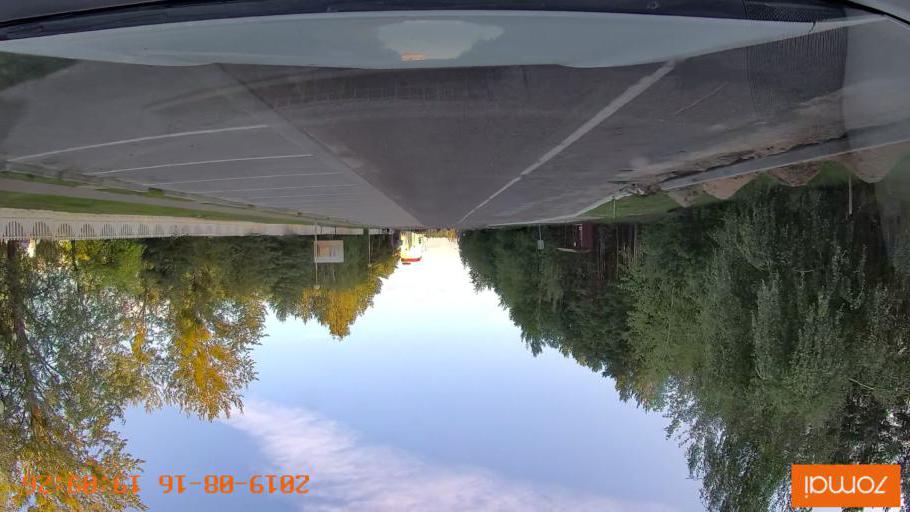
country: BY
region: Mogilev
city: Asipovichy
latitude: 53.3180
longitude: 28.6345
